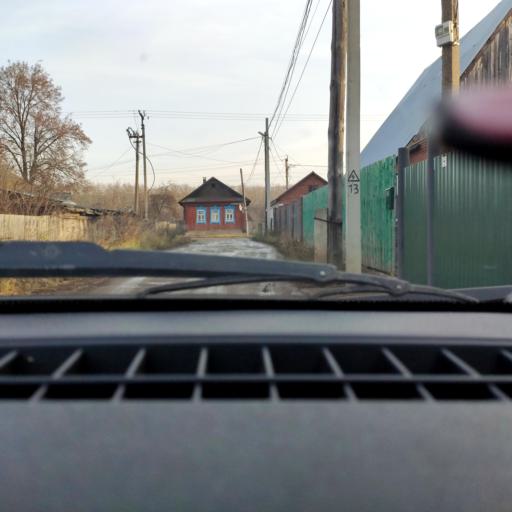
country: RU
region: Bashkortostan
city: Iglino
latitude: 54.8221
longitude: 56.1850
